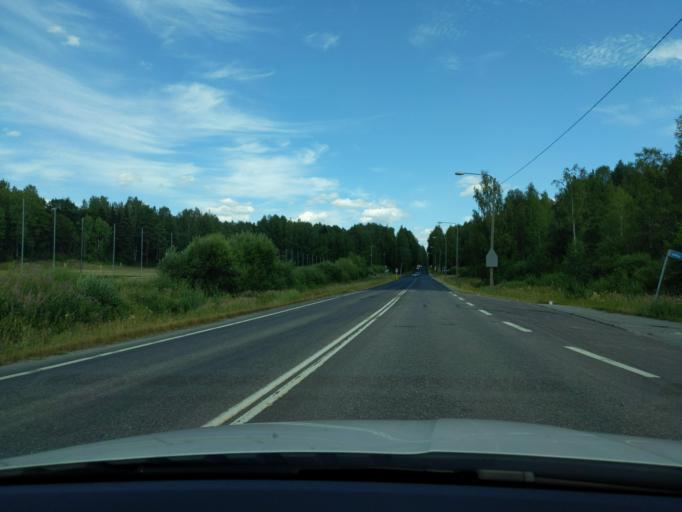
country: FI
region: Paijanne Tavastia
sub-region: Lahti
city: Lahti
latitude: 61.0258
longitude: 25.7287
